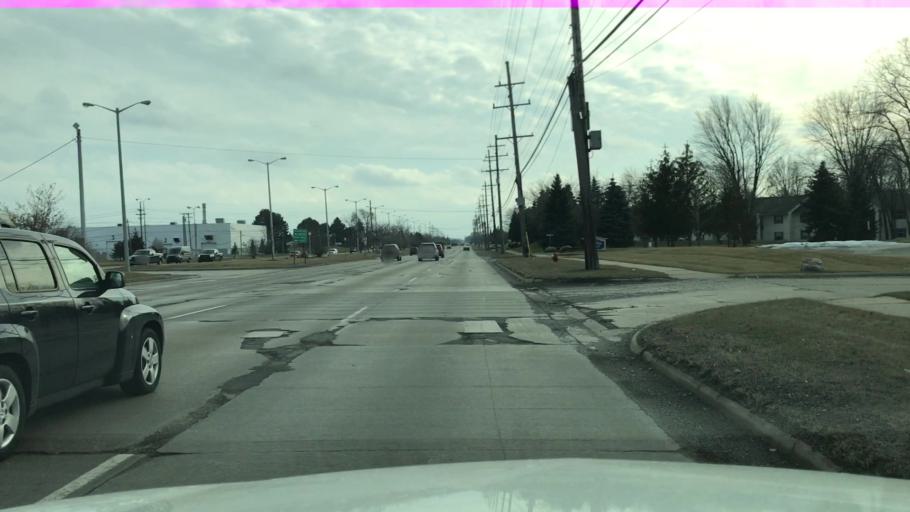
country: US
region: Michigan
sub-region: Macomb County
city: Sterling Heights
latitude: 42.5636
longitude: -83.0495
